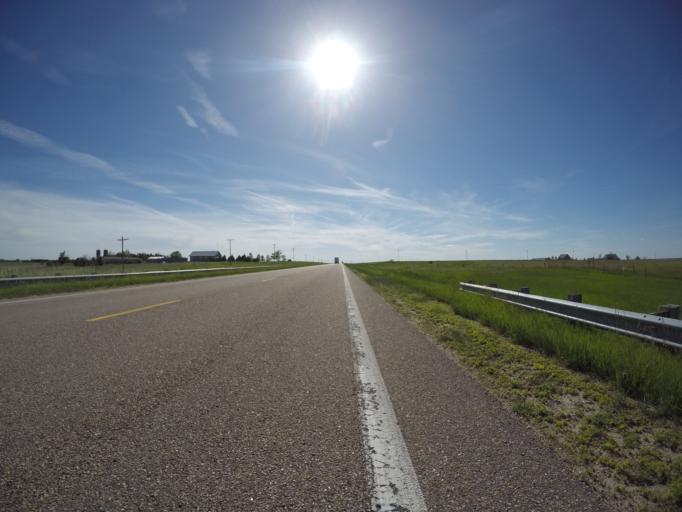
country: US
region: Kansas
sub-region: Cheyenne County
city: Saint Francis
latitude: 39.7566
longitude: -102.0288
